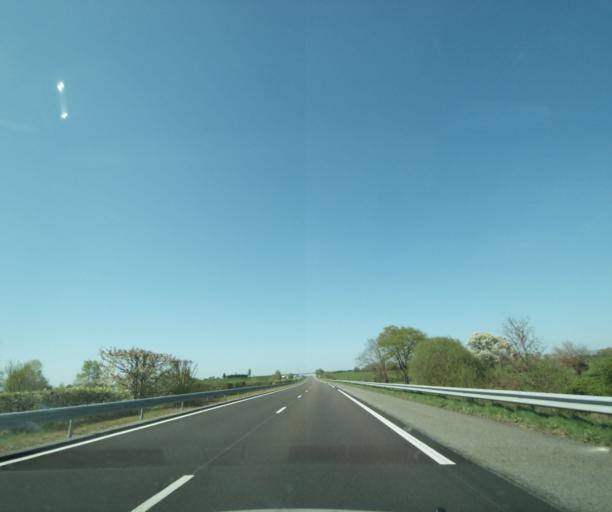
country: FR
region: Bourgogne
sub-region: Departement de la Nievre
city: Neuvy-sur-Loire
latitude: 47.5180
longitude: 2.9152
